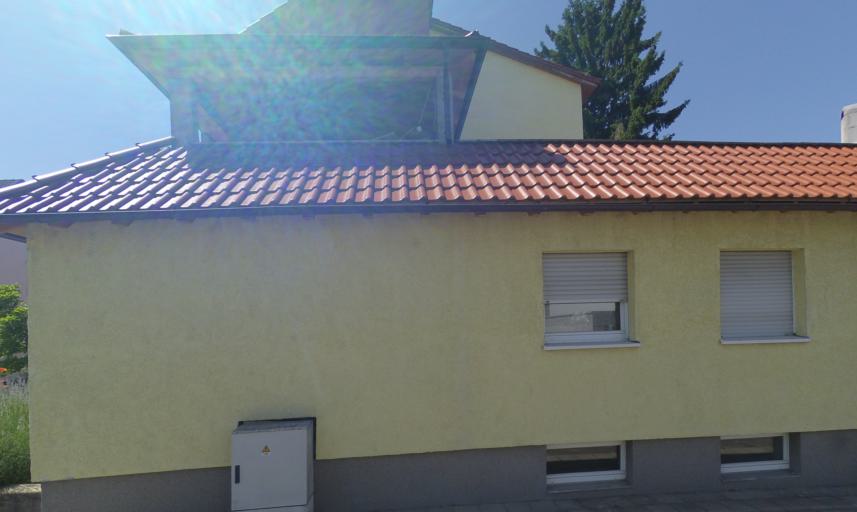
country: DE
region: Rheinland-Pfalz
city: Otterstadt
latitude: 49.3738
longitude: 8.4502
